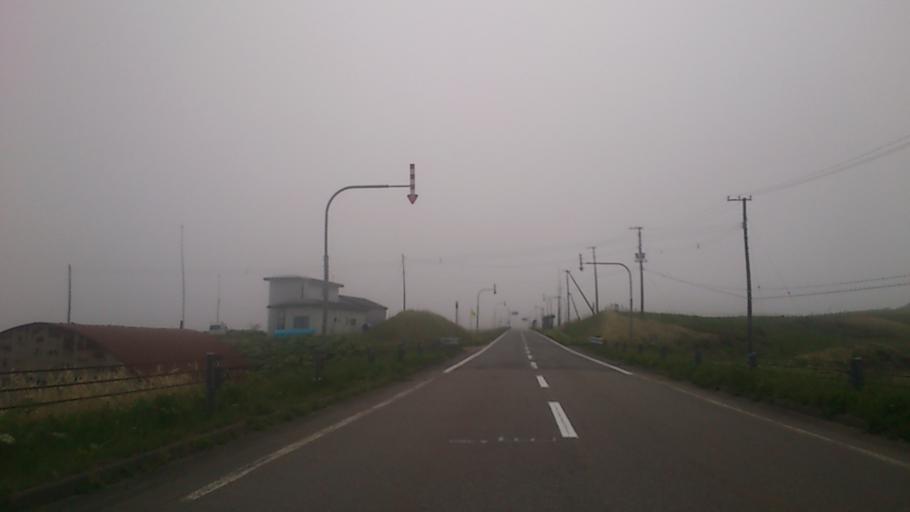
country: JP
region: Hokkaido
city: Nemuro
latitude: 43.1718
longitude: 145.2852
